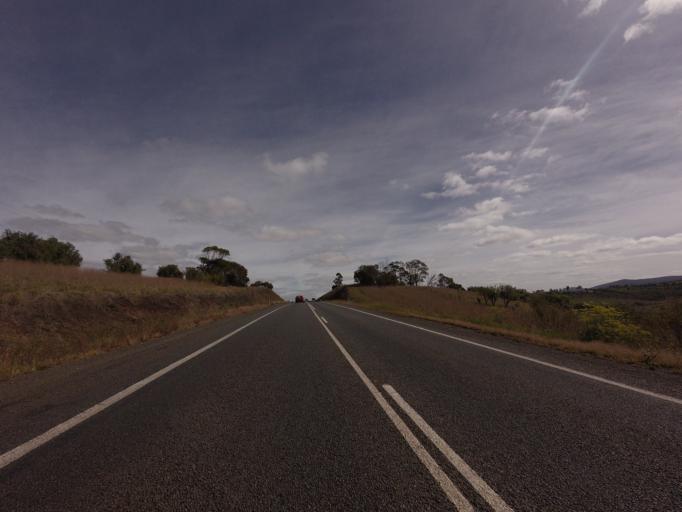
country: AU
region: Tasmania
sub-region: Sorell
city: Sorell
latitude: -42.7828
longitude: 147.5890
